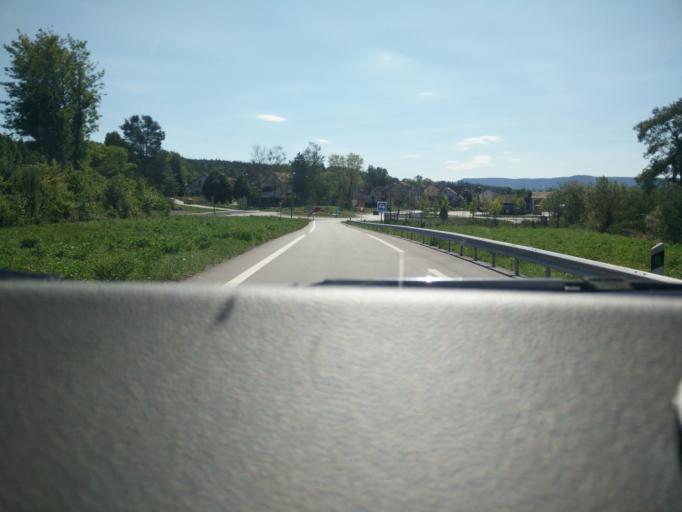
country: FR
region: Lorraine
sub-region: Departement des Vosges
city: Etival-Clairefontaine
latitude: 48.3746
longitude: 6.8765
